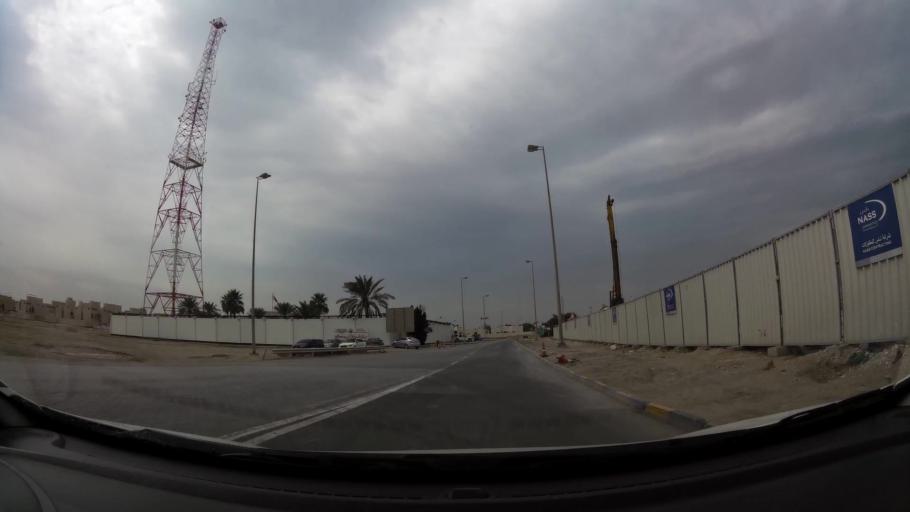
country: BH
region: Manama
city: Manama
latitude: 26.1837
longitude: 50.5899
